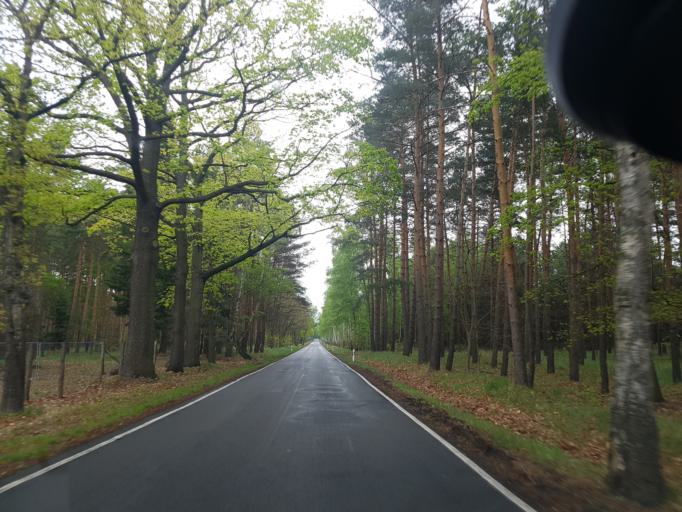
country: DE
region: Brandenburg
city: Spremberg
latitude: 51.6193
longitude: 14.4152
